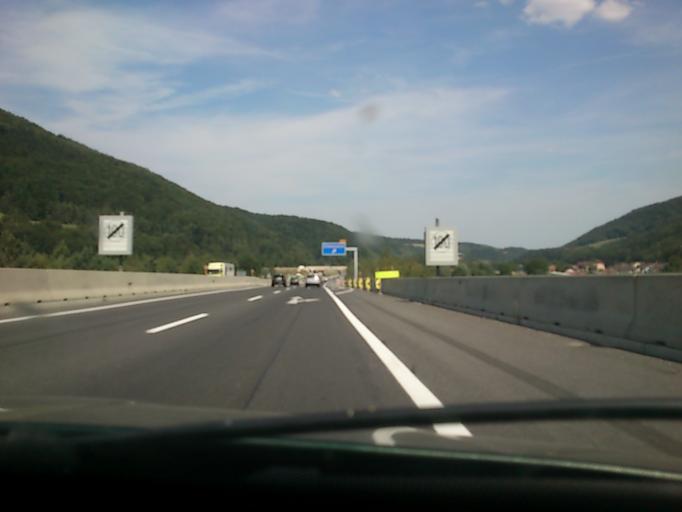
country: AT
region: Lower Austria
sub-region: Politischer Bezirk Neunkirchen
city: Grimmenstein
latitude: 47.6269
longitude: 16.1319
